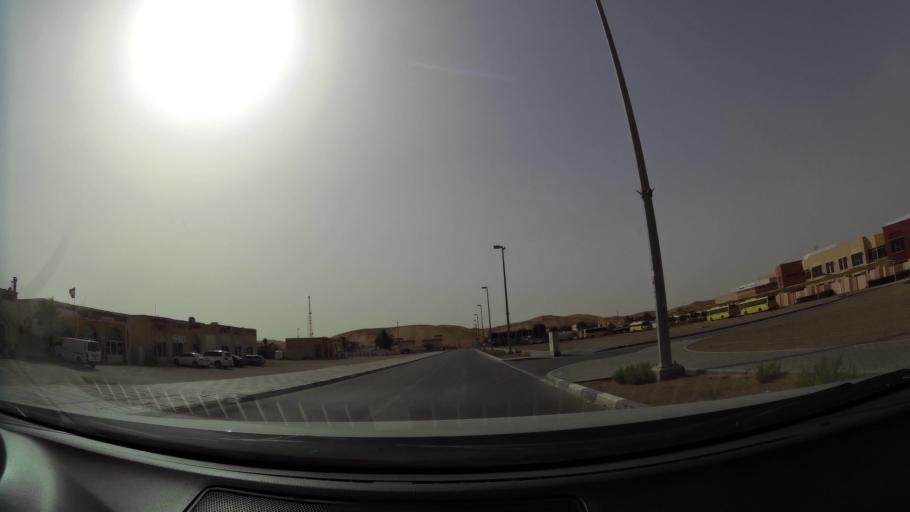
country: AE
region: Abu Dhabi
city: Al Ain
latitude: 24.2085
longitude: 55.5835
